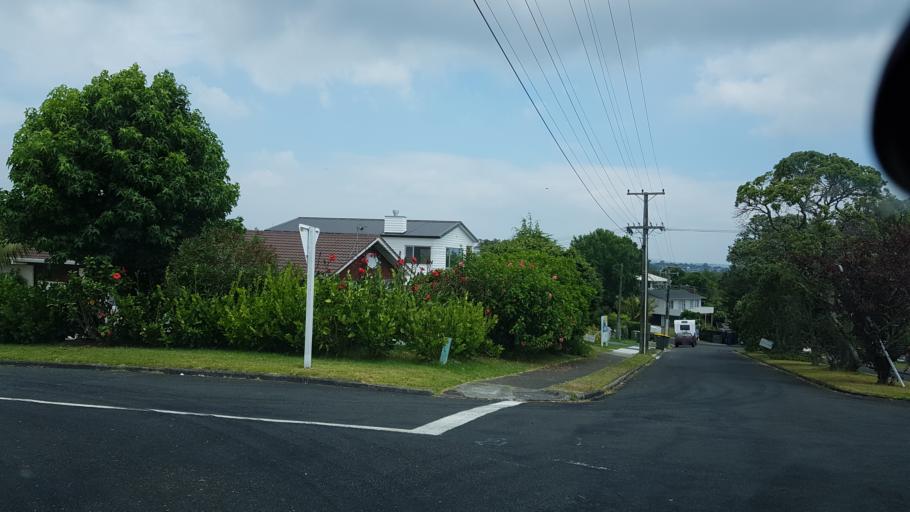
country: NZ
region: Auckland
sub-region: Auckland
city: North Shore
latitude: -36.8000
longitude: 174.7842
